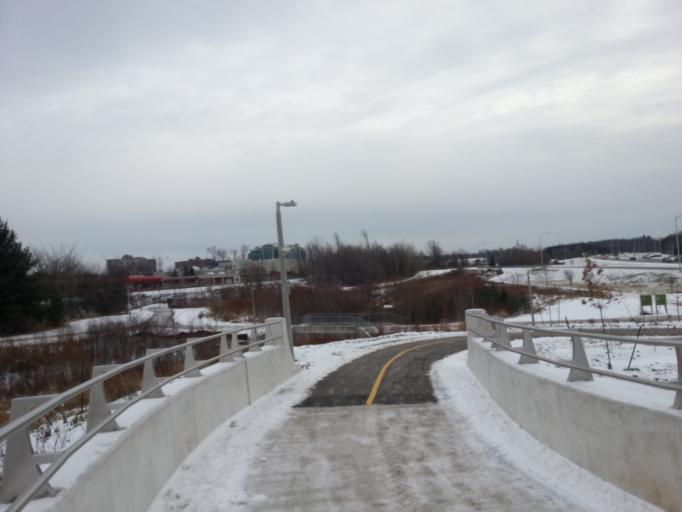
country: CA
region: Ontario
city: Ottawa
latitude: 45.3543
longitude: -75.6573
